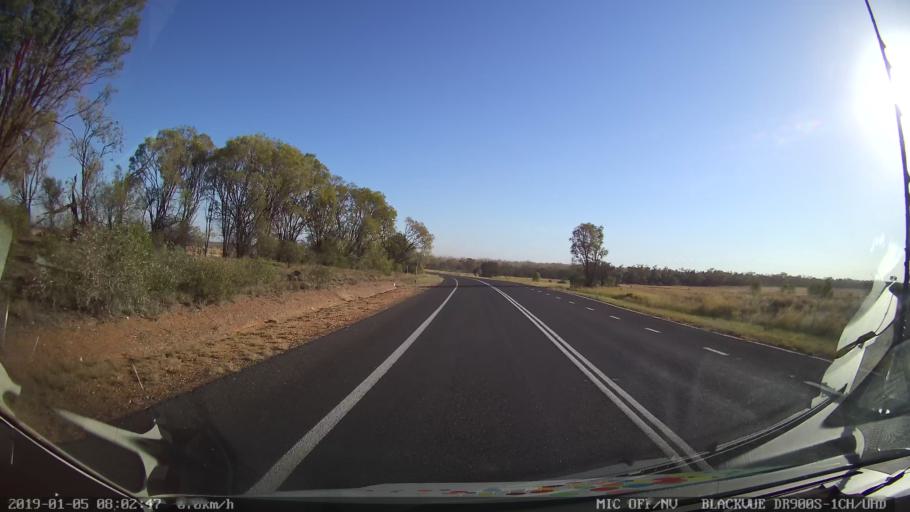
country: AU
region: New South Wales
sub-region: Gilgandra
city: Gilgandra
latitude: -31.6726
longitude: 148.7146
